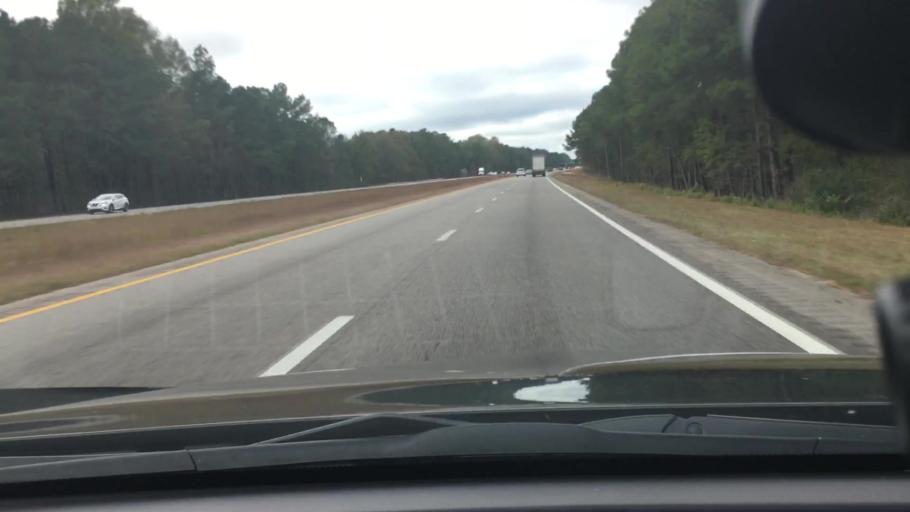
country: US
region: North Carolina
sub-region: Wilson County
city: Lucama
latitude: 35.7781
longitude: -78.0739
